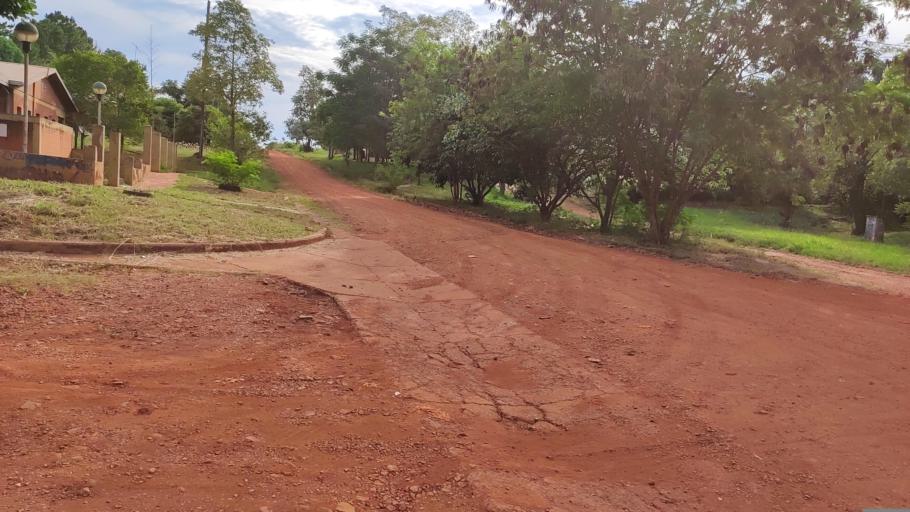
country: AR
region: Misiones
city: Gobernador Roca
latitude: -27.1493
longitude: -55.5327
